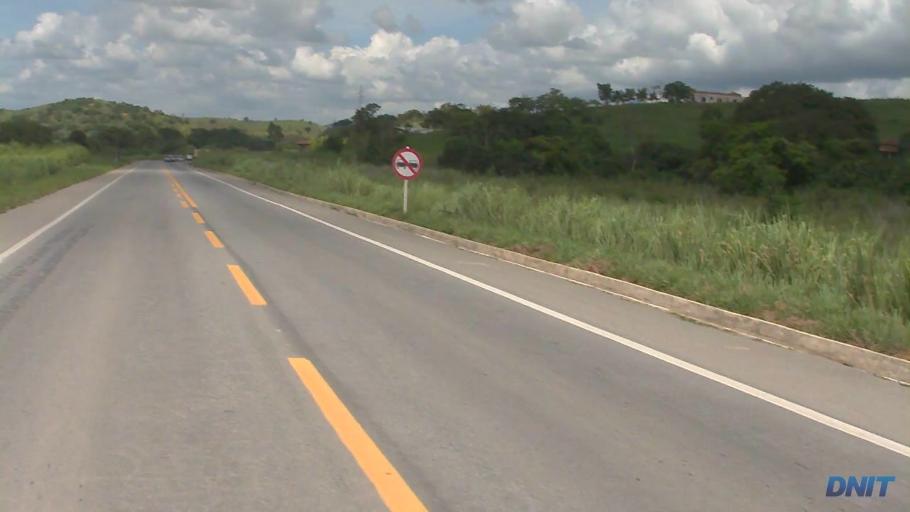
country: BR
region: Minas Gerais
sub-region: Governador Valadares
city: Governador Valadares
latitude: -18.9868
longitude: -42.1097
